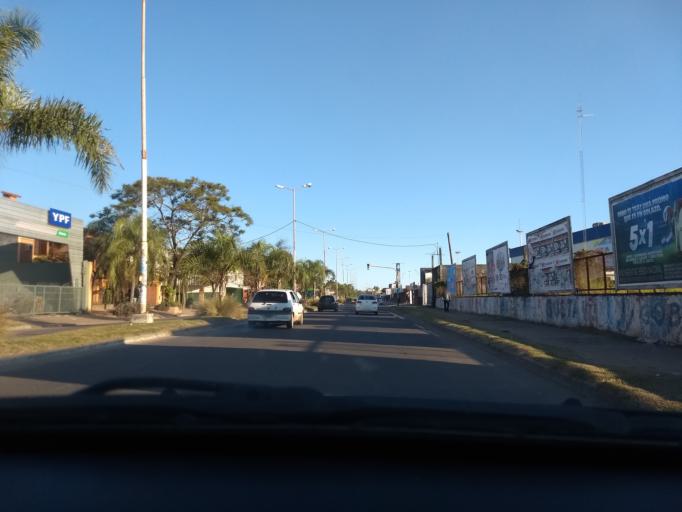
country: AR
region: Corrientes
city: Corrientes
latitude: -27.4760
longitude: -58.8141
